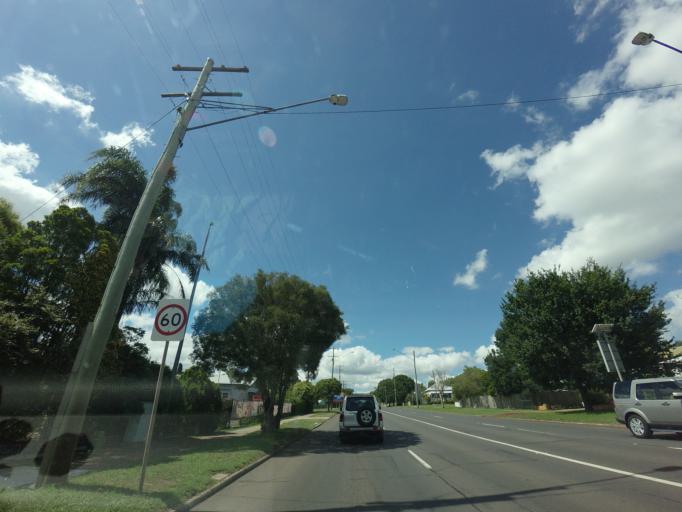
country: AU
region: Queensland
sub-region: Toowoomba
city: East Toowoomba
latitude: -27.5706
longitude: 151.9748
